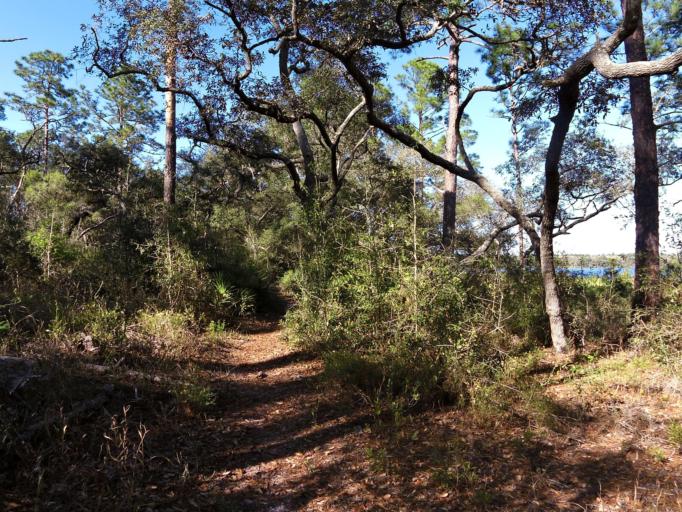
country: US
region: Florida
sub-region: Clay County
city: Keystone Heights
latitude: 29.8235
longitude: -82.0236
